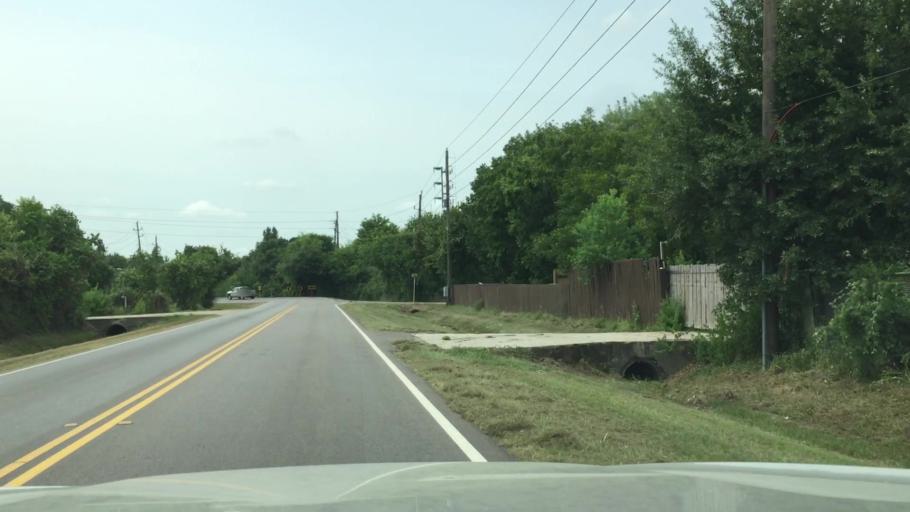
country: US
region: Texas
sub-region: Harris County
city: Jersey Village
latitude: 29.9169
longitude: -95.5479
